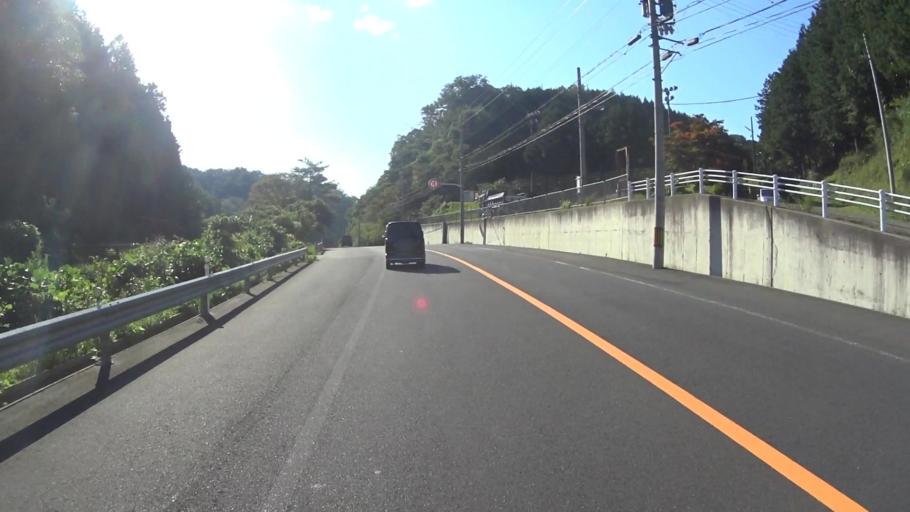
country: JP
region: Kyoto
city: Miyazu
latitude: 35.6590
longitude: 135.0042
